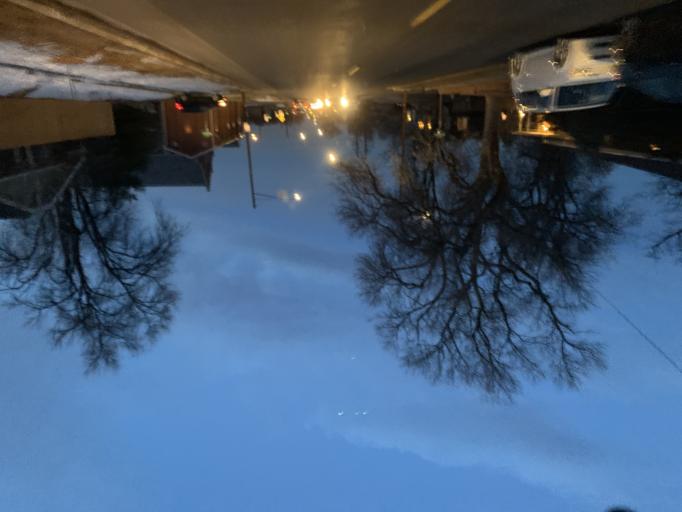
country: US
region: Colorado
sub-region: Adams County
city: Berkley
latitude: 39.7767
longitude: -105.0411
